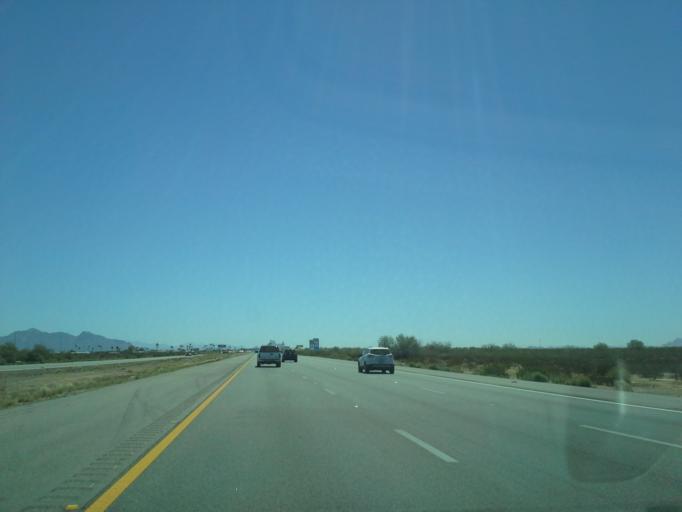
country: US
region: Arizona
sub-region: Pinal County
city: Arizona City
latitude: 32.7880
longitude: -111.6371
